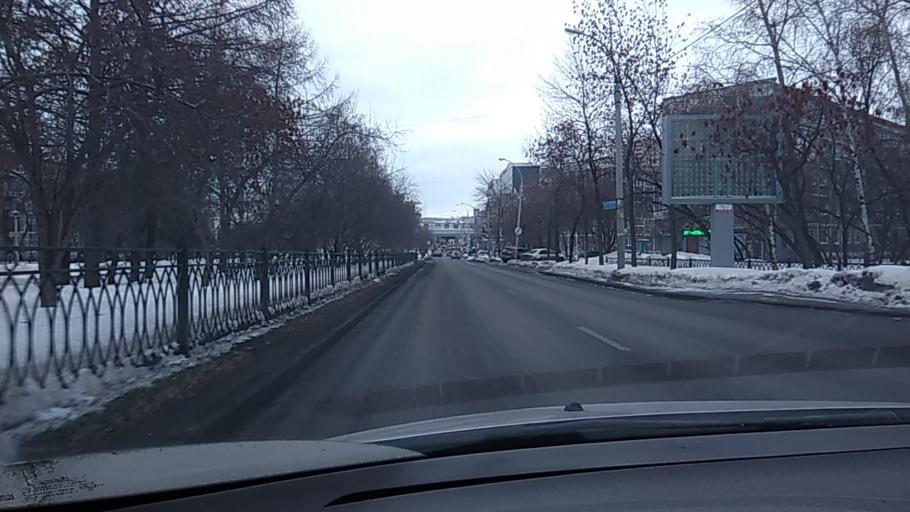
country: RU
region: Sverdlovsk
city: Yekaterinburg
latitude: 56.8181
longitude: 60.5829
